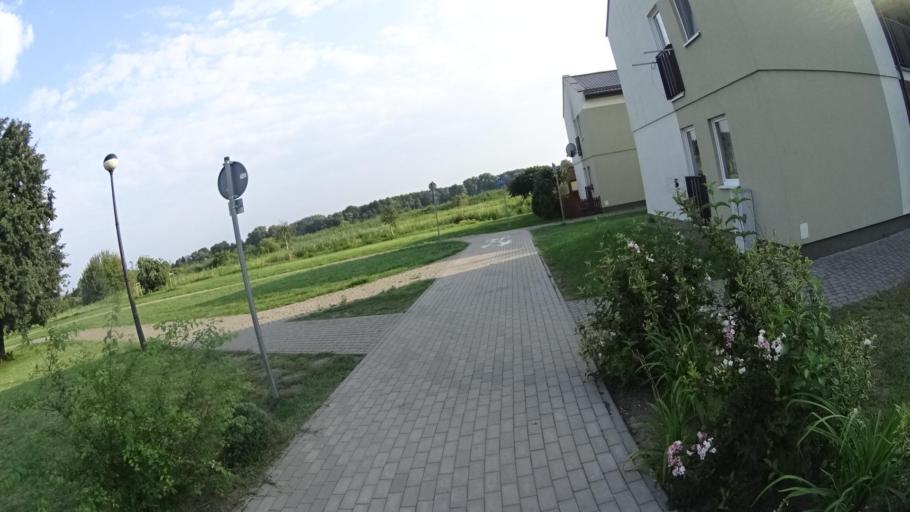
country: PL
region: Masovian Voivodeship
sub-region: Powiat pruszkowski
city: Raszyn
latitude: 52.1503
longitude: 20.9211
